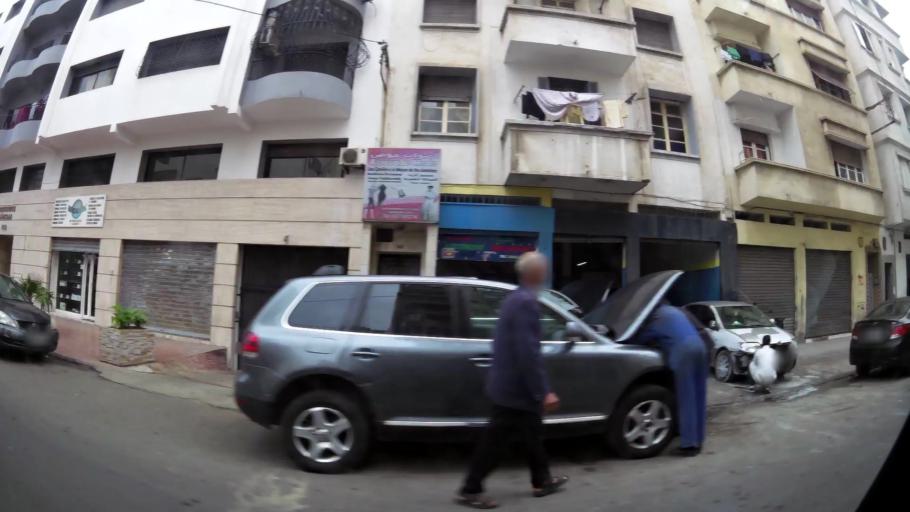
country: MA
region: Grand Casablanca
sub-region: Casablanca
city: Casablanca
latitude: 33.6013
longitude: -7.6340
